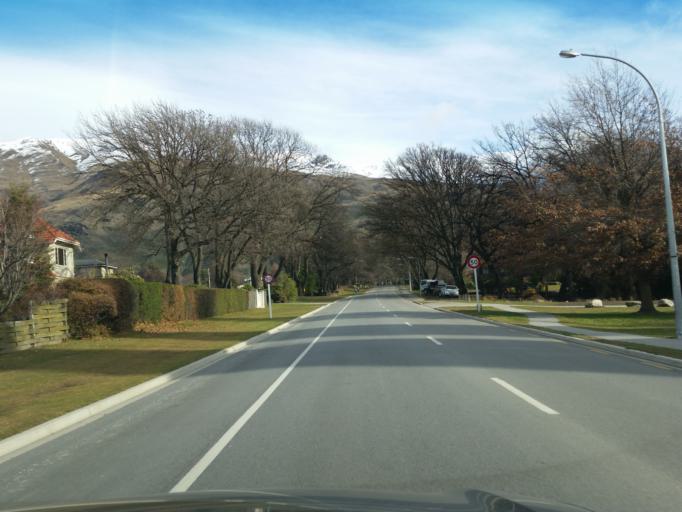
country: NZ
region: Otago
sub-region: Queenstown-Lakes District
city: Wanaka
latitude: -44.7004
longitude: 169.1205
